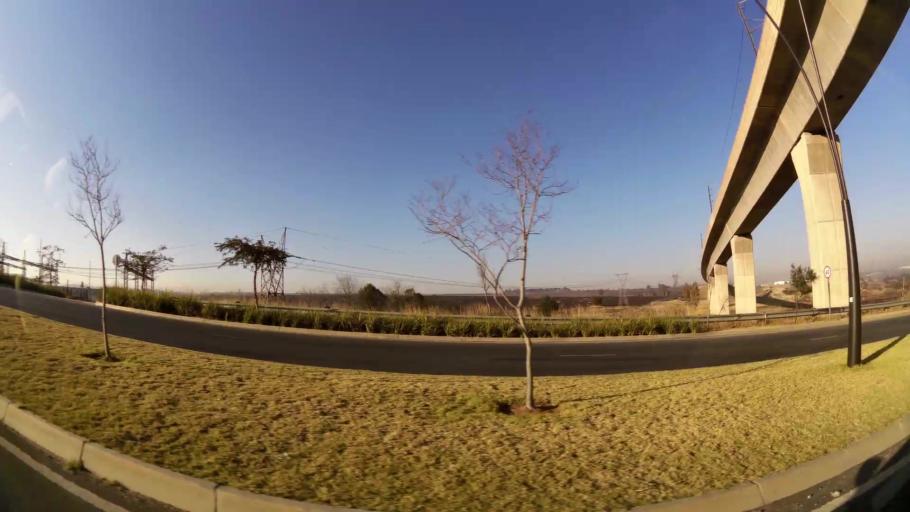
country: ZA
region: Gauteng
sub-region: City of Johannesburg Metropolitan Municipality
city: Midrand
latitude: -26.0260
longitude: 28.1283
